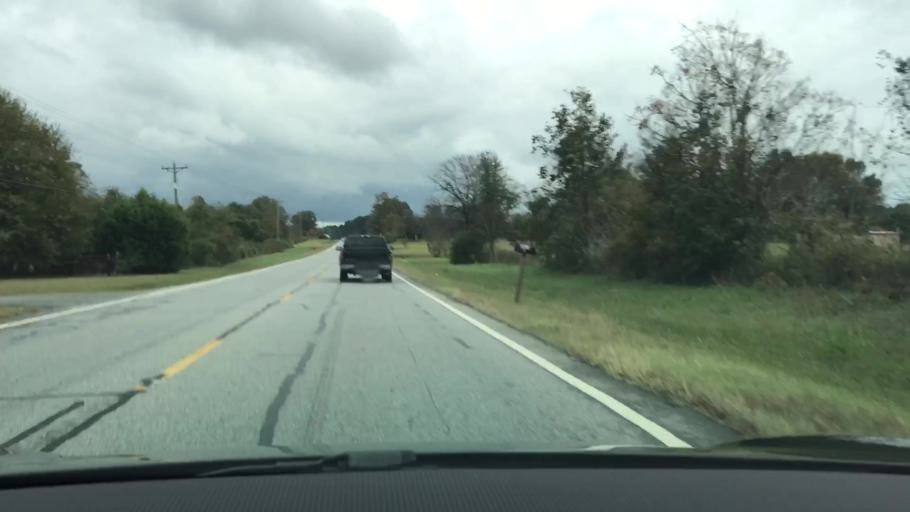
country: US
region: Georgia
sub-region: Oconee County
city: Watkinsville
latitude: 33.8207
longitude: -83.3669
